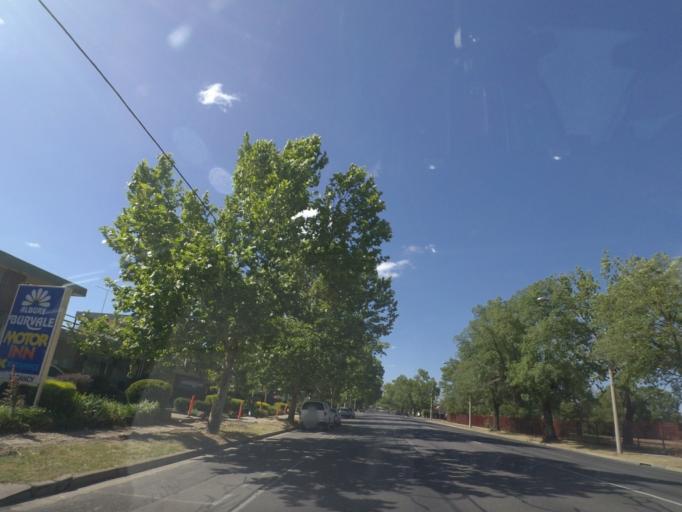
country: AU
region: New South Wales
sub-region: Albury Municipality
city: Albury
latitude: -36.0728
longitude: 146.9257
